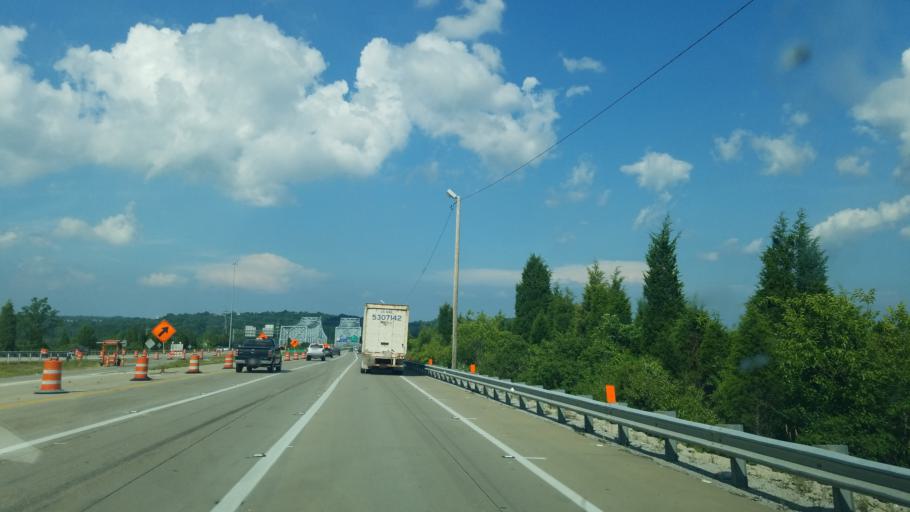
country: US
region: Kentucky
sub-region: Campbell County
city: Fort Thomas
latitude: 39.0538
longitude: -84.4379
